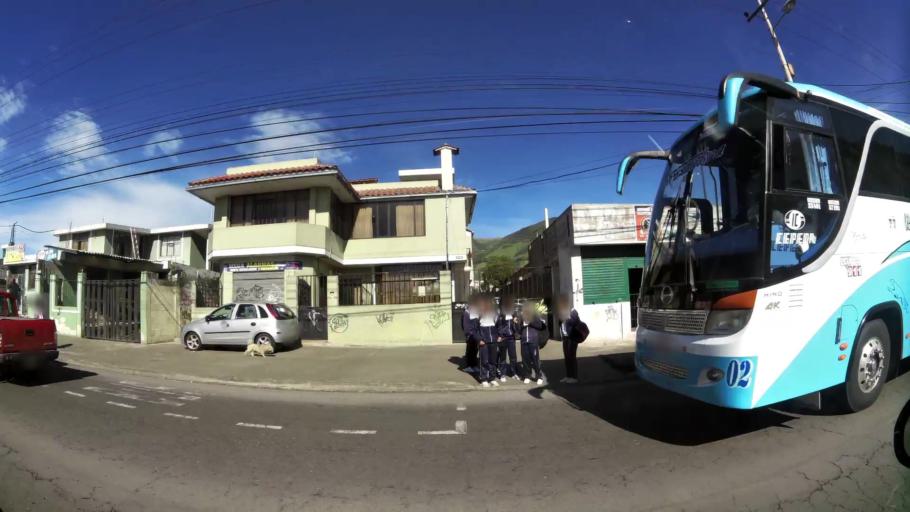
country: EC
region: Pichincha
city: Quito
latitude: -0.3179
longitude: -78.5577
